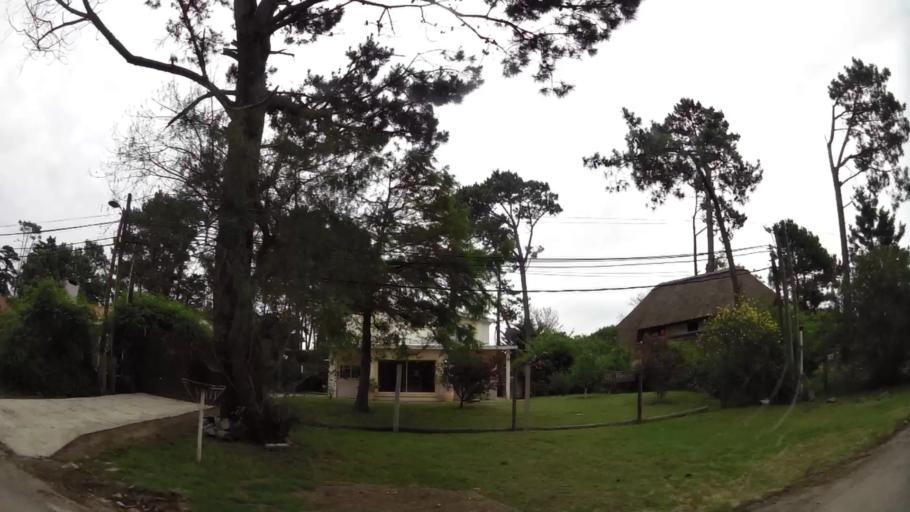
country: UY
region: Maldonado
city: Maldonado
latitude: -34.9098
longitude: -54.9754
